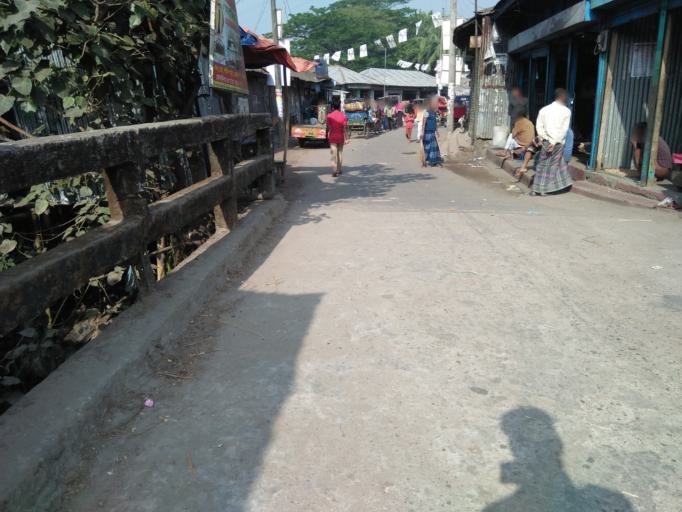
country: BD
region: Khulna
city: Uttar Char Fasson
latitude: 22.1927
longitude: 90.6732
